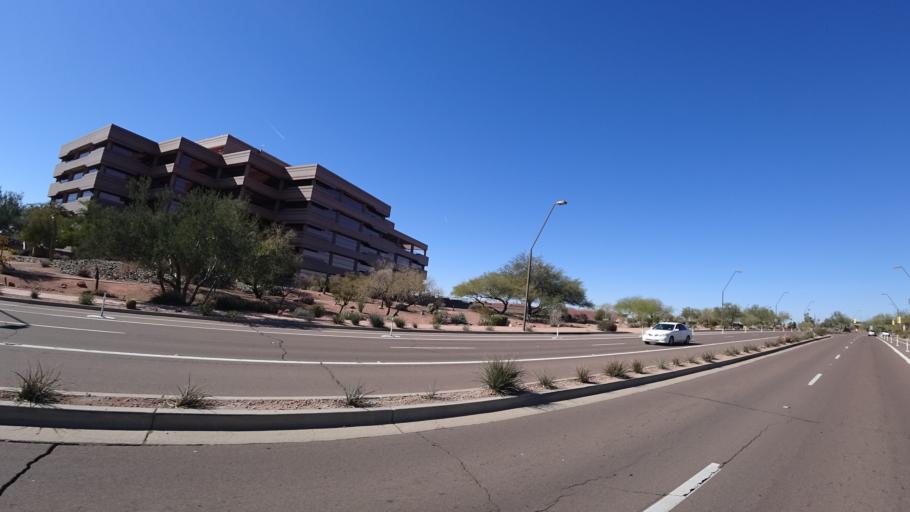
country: US
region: Arizona
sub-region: Maricopa County
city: Tempe Junction
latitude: 33.4471
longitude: -111.9552
